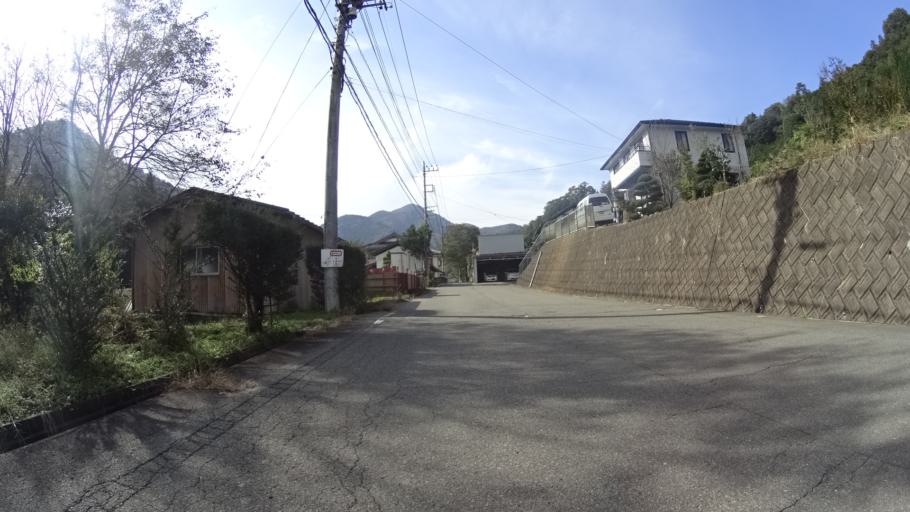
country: JP
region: Yamanashi
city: Otsuki
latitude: 35.5960
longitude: 138.9707
